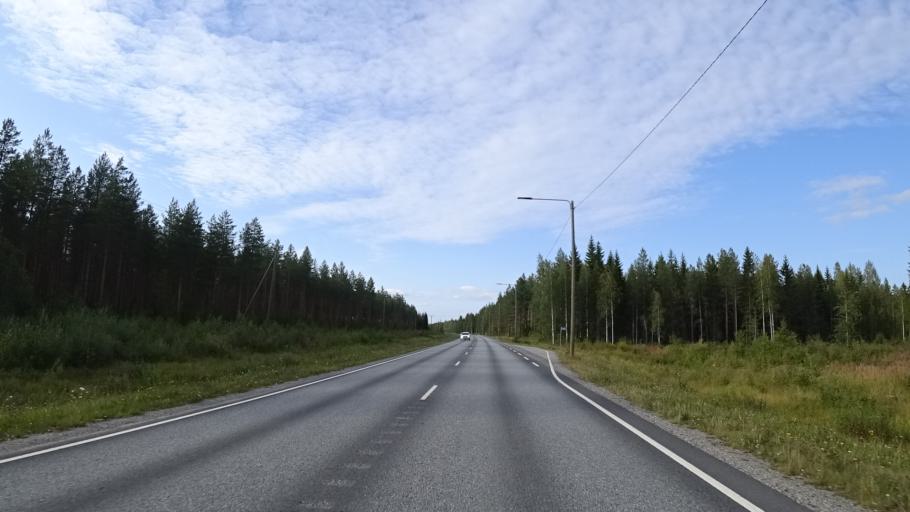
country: FI
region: North Karelia
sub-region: Joensuu
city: Eno
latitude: 62.8725
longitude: 30.2022
